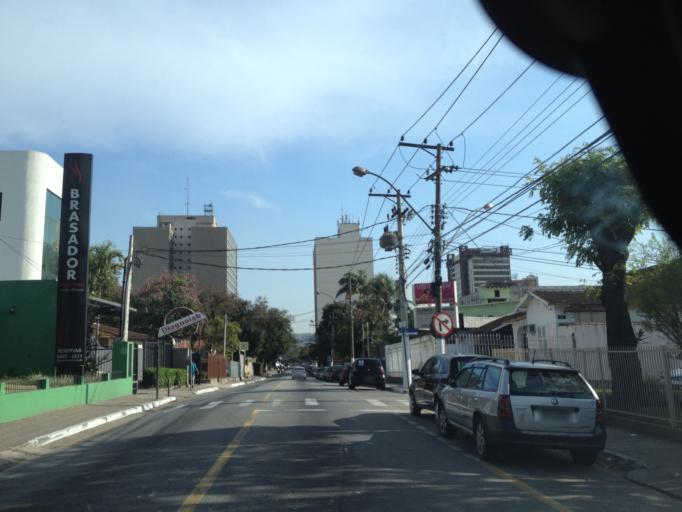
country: BR
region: Rio de Janeiro
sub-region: Volta Redonda
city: Volta Redonda
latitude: -22.5209
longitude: -44.1075
